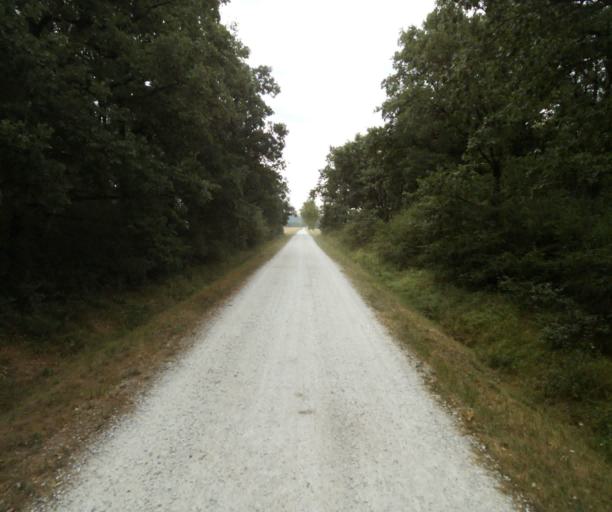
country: FR
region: Midi-Pyrenees
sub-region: Departement de la Haute-Garonne
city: Saint-Felix-Lauragais
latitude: 43.4401
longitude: 1.9392
